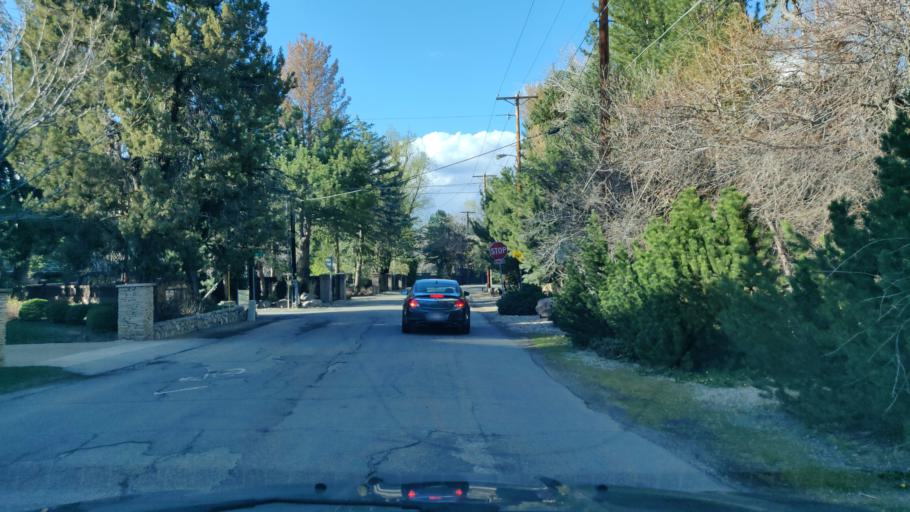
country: US
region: Utah
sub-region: Salt Lake County
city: Cottonwood Heights
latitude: 40.6419
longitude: -111.8248
